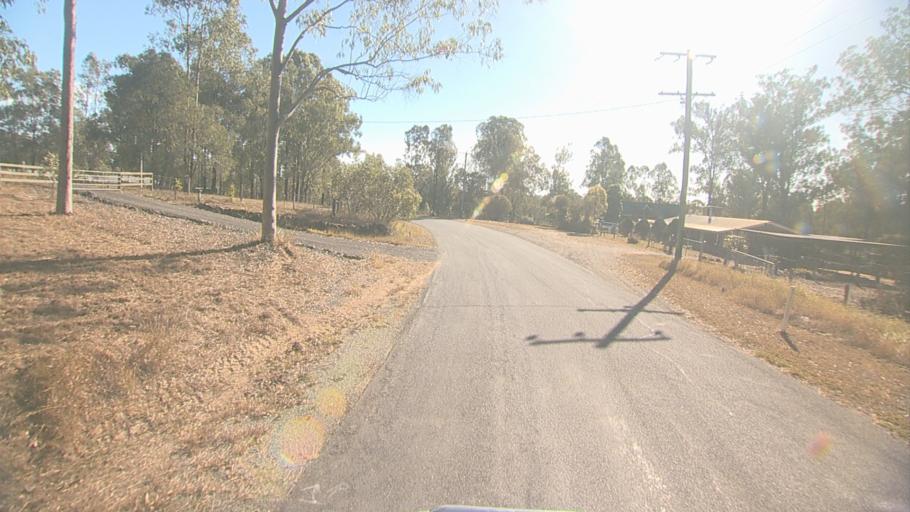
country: AU
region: Queensland
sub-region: Logan
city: Cedar Vale
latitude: -27.8520
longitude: 152.9939
